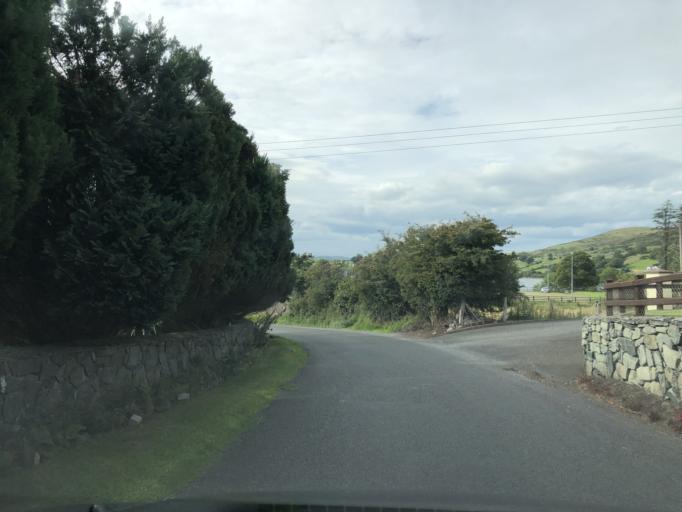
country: GB
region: Northern Ireland
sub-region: Down District
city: Castlewellan
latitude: 54.2336
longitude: -6.0121
